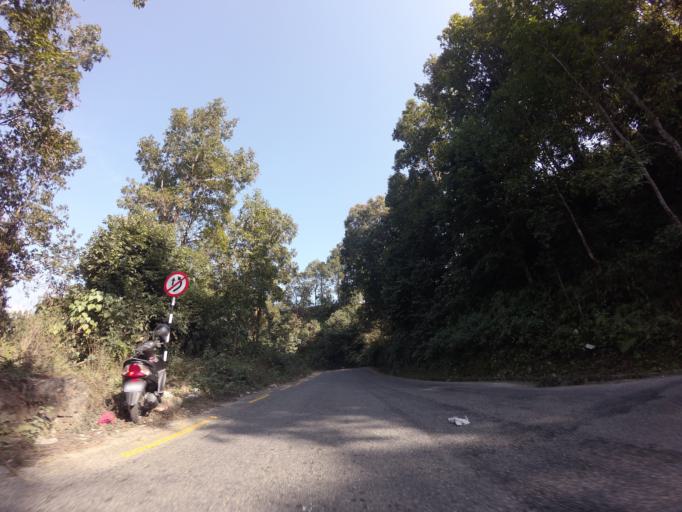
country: NP
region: Western Region
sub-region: Gandaki Zone
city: Pokhara
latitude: 28.1879
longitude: 83.9027
